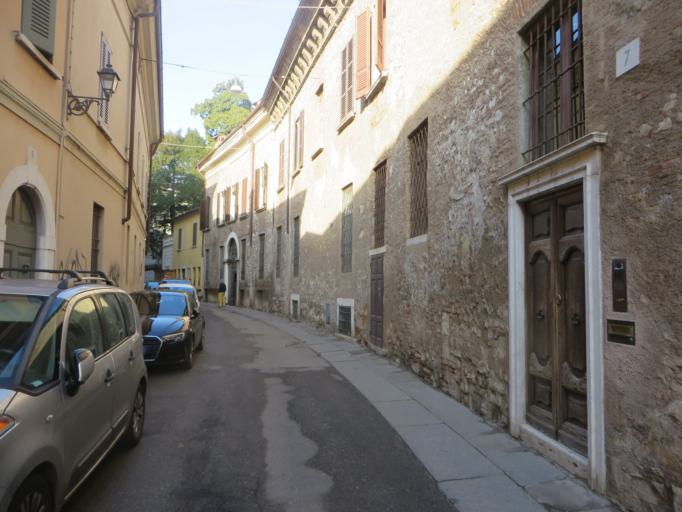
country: IT
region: Lombardy
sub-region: Provincia di Brescia
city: Brescia
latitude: 45.5340
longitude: 10.2269
